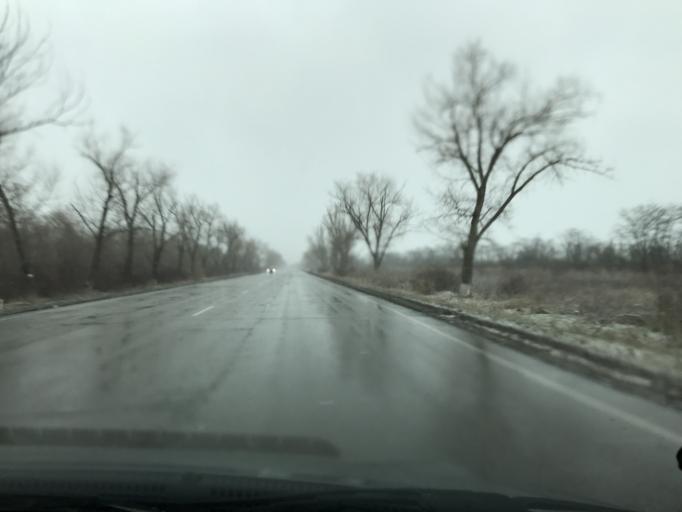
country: RU
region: Rostov
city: Kirovskaya
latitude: 47.0093
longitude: 39.9437
